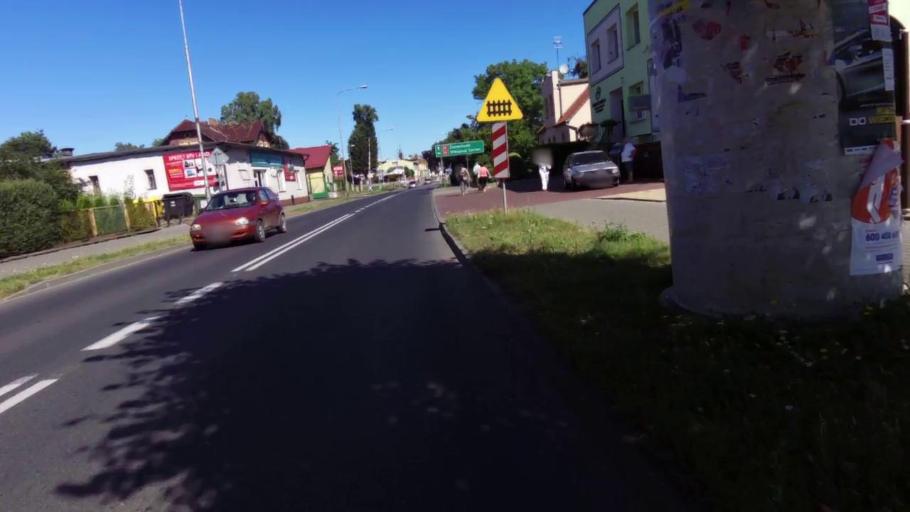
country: PL
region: West Pomeranian Voivodeship
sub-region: Powiat drawski
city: Zlocieniec
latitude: 53.5281
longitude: 16.0124
